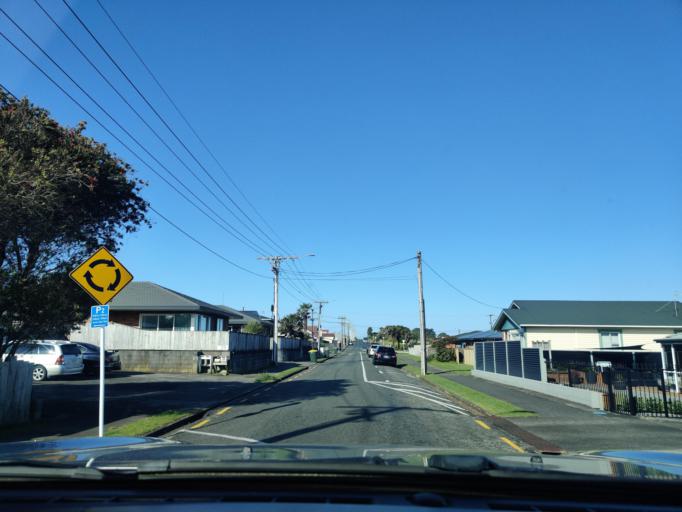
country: NZ
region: Taranaki
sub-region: New Plymouth District
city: New Plymouth
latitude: -39.0487
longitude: 174.1042
